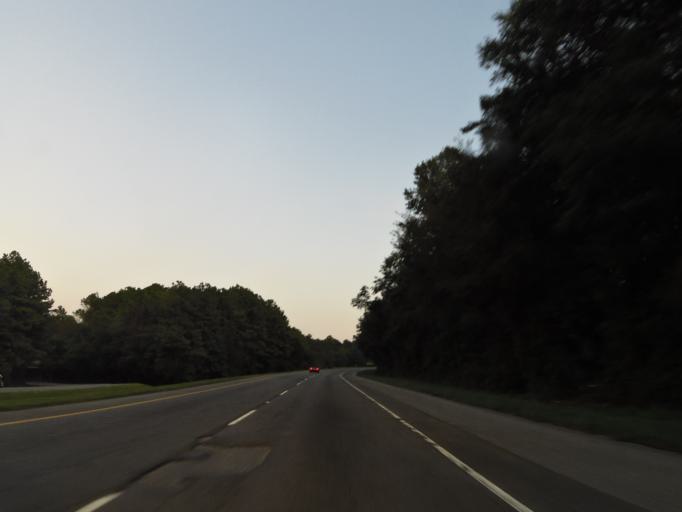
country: US
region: Tennessee
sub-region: Anderson County
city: Oak Ridge
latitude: 35.9789
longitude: -84.1808
